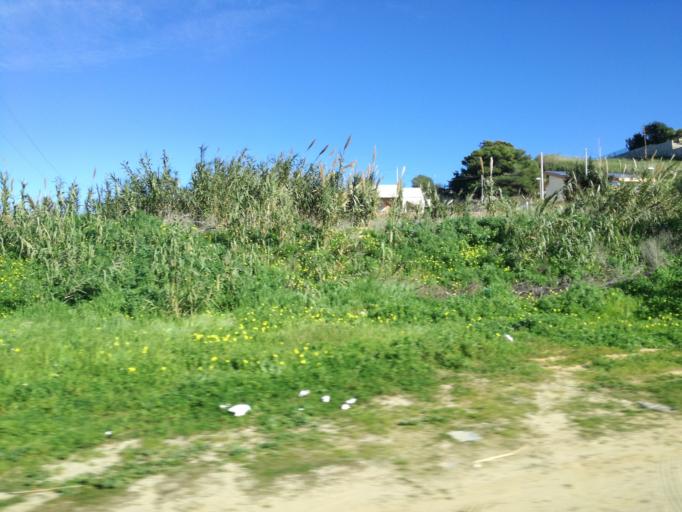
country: IT
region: Sicily
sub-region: Provincia di Caltanissetta
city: Gela
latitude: 37.0906
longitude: 14.1786
